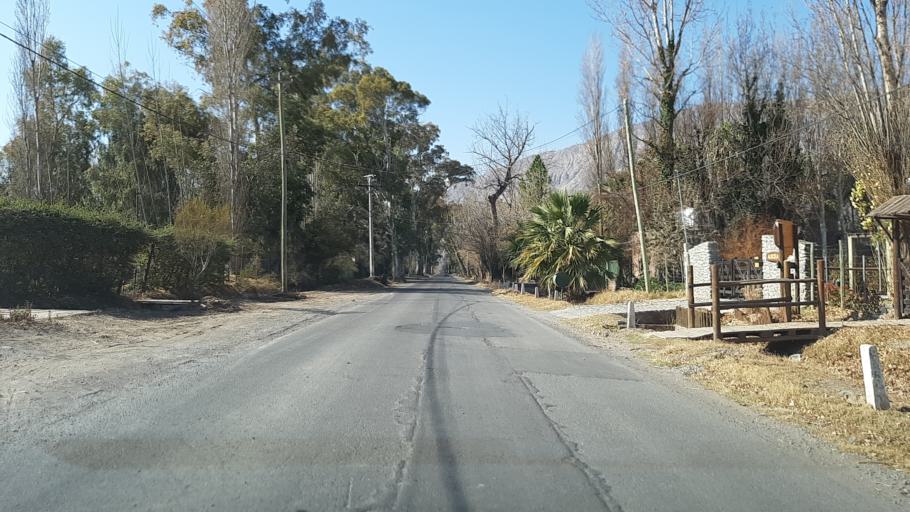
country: AR
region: San Juan
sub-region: Departamento de Zonda
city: Zonda
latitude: -31.5608
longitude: -68.7257
